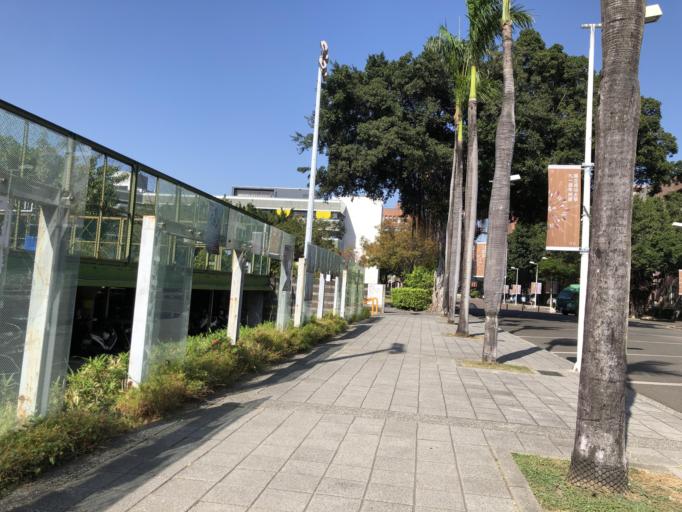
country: TW
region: Taiwan
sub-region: Tainan
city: Tainan
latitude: 22.9969
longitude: 120.2167
